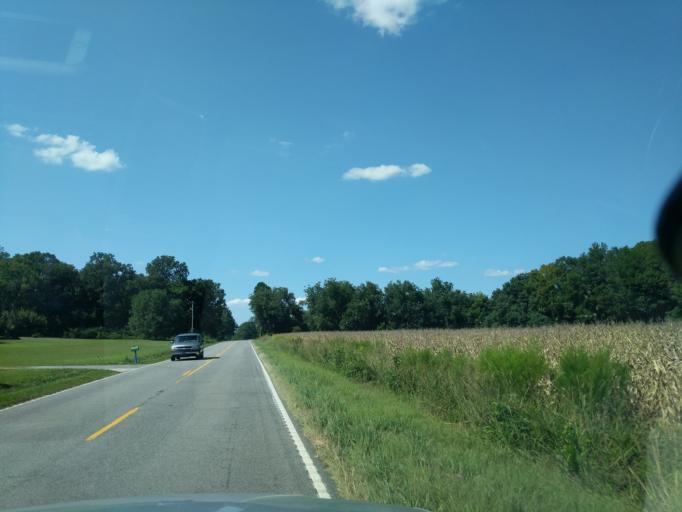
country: US
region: South Carolina
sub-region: Lexington County
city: Leesville
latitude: 34.0122
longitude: -81.5178
